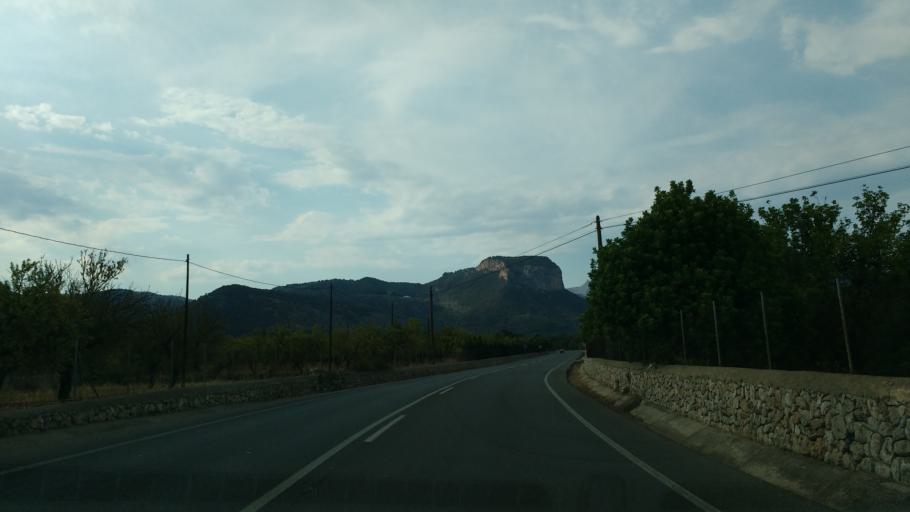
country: ES
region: Balearic Islands
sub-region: Illes Balears
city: Alaro
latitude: 39.6917
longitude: 2.8039
